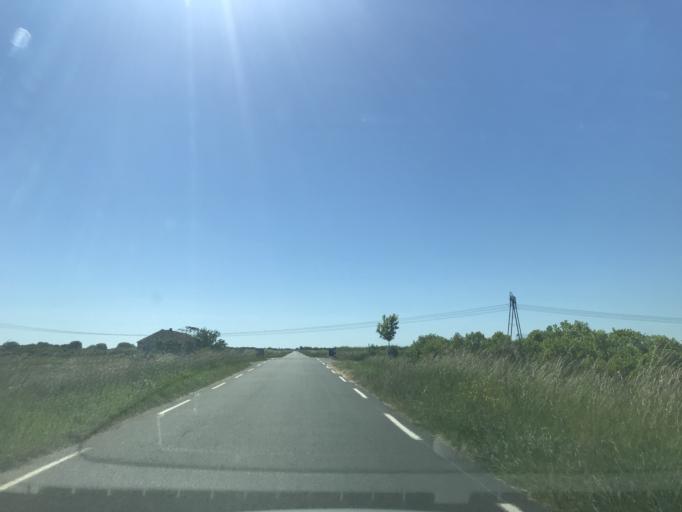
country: FR
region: Aquitaine
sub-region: Departement de la Gironde
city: Saint-Ciers-sur-Gironde
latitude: 45.2890
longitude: -0.6557
